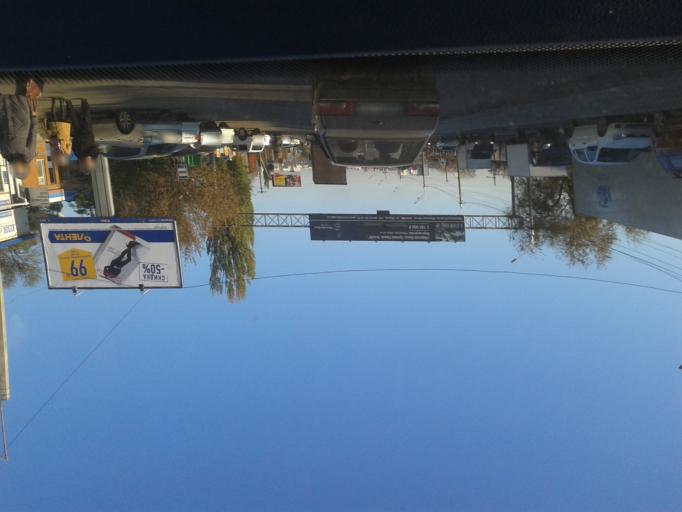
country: RU
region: Volgograd
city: Volgograd
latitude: 48.6963
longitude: 44.4687
